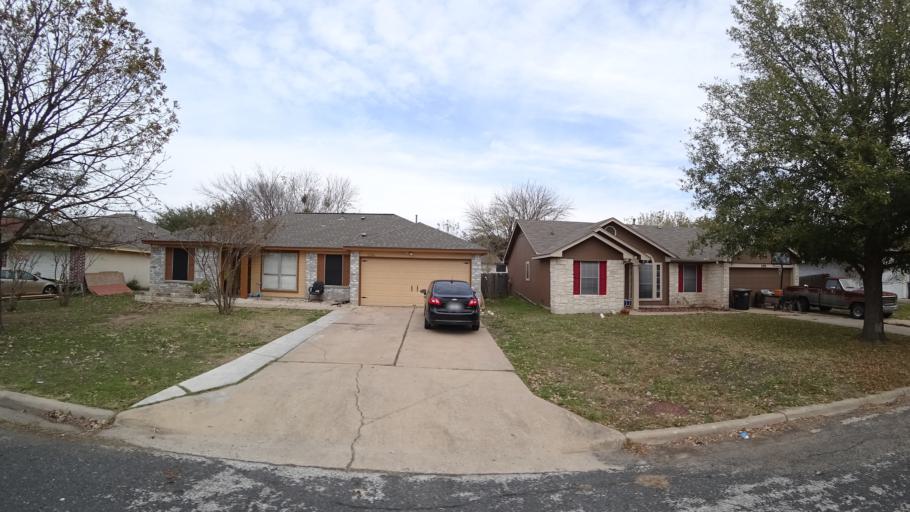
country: US
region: Texas
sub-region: Travis County
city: Garfield
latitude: 30.1575
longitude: -97.6467
